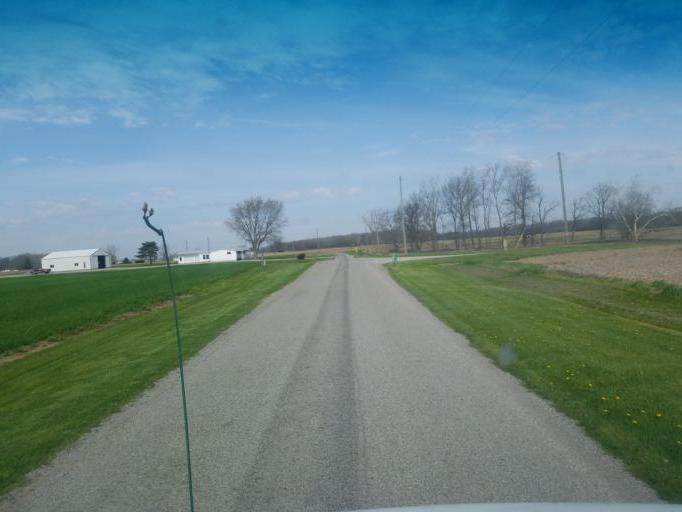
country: US
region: Ohio
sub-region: Union County
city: Richwood
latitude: 40.4846
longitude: -83.4487
